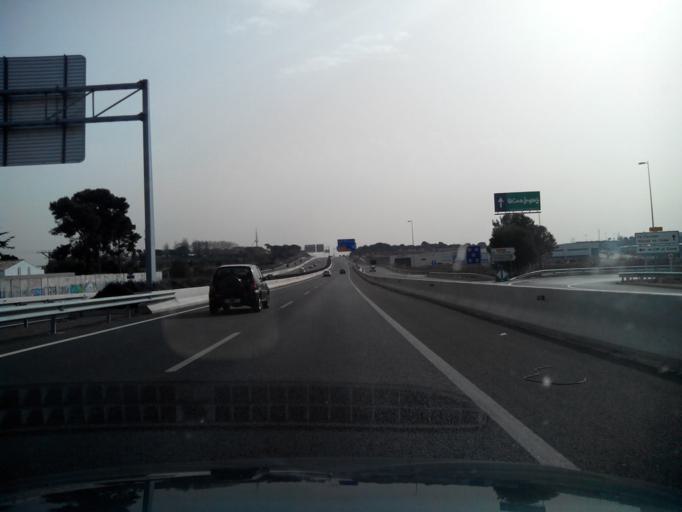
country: ES
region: Catalonia
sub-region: Provincia de Tarragona
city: Vila-seca
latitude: 41.1341
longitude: 1.1801
